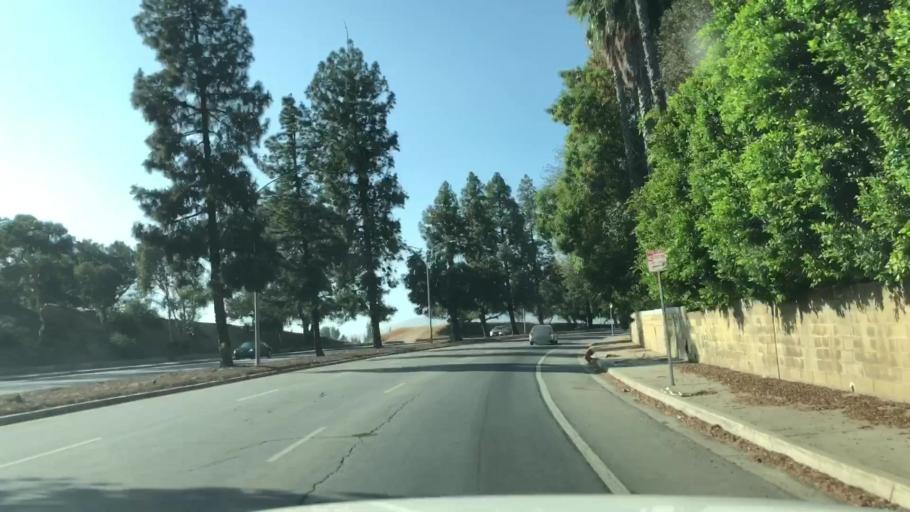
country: US
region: California
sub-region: Los Angeles County
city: Northridge
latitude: 34.2610
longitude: -118.5562
